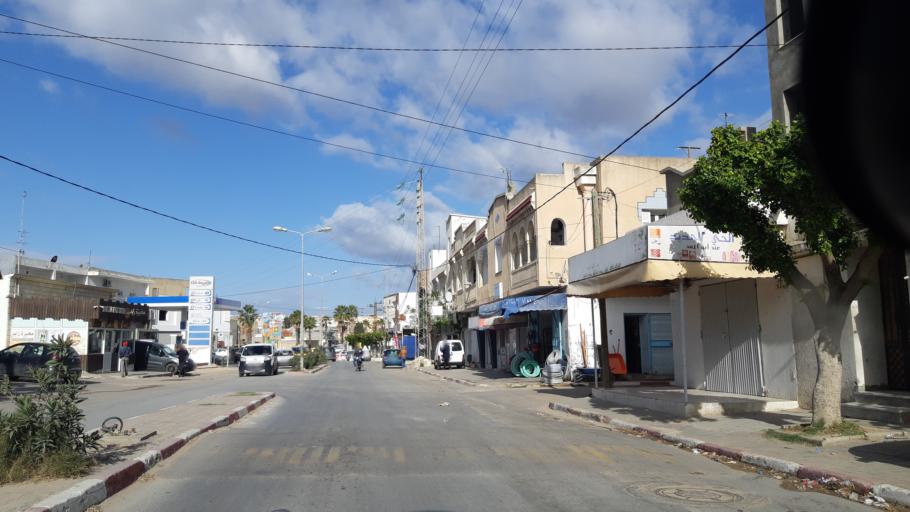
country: TN
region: Susah
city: Akouda
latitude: 35.8691
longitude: 10.5472
